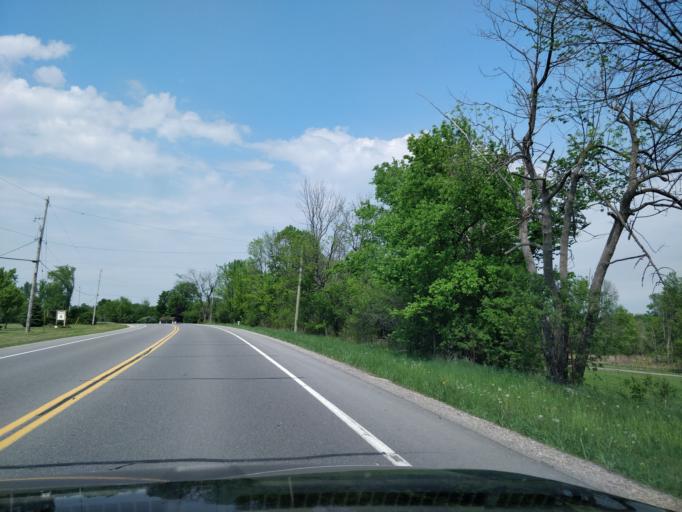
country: CA
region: Ontario
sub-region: Lanark County
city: Smiths Falls
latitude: 45.0110
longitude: -76.0802
